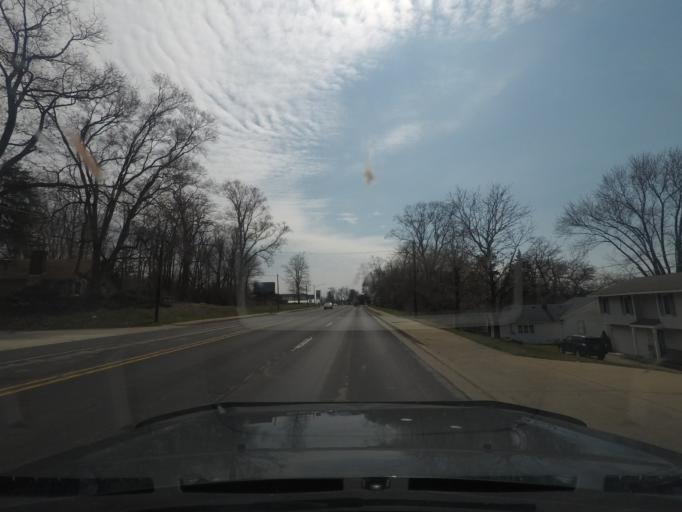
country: US
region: Indiana
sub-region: LaPorte County
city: LaPorte
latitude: 41.6272
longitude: -86.7379
